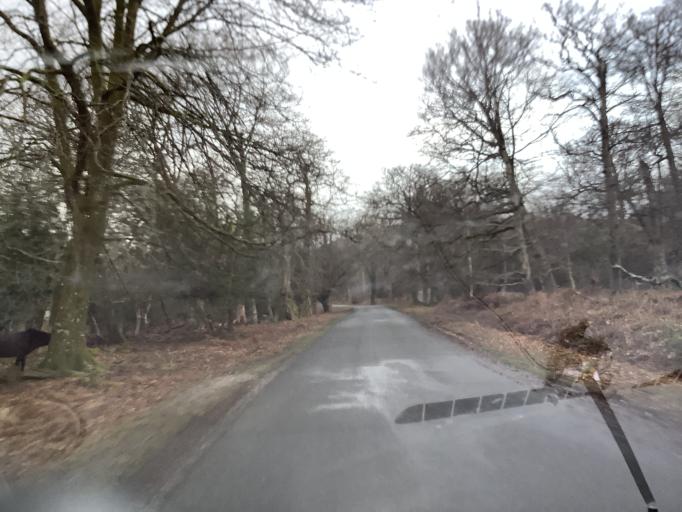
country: GB
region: England
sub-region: Hampshire
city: Lyndhurst
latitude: 50.8698
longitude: -1.6453
